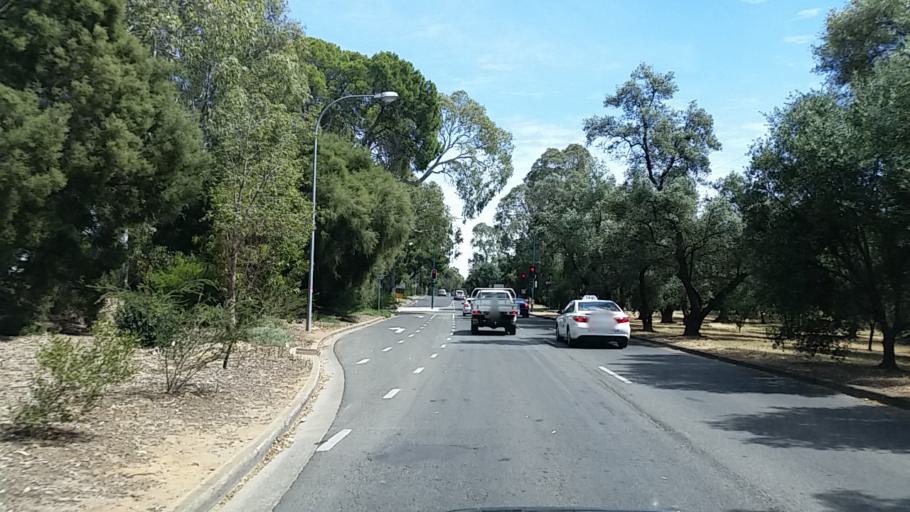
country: AU
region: South Australia
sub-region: Adelaide
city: North Adelaide
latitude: -34.9056
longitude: 138.6116
